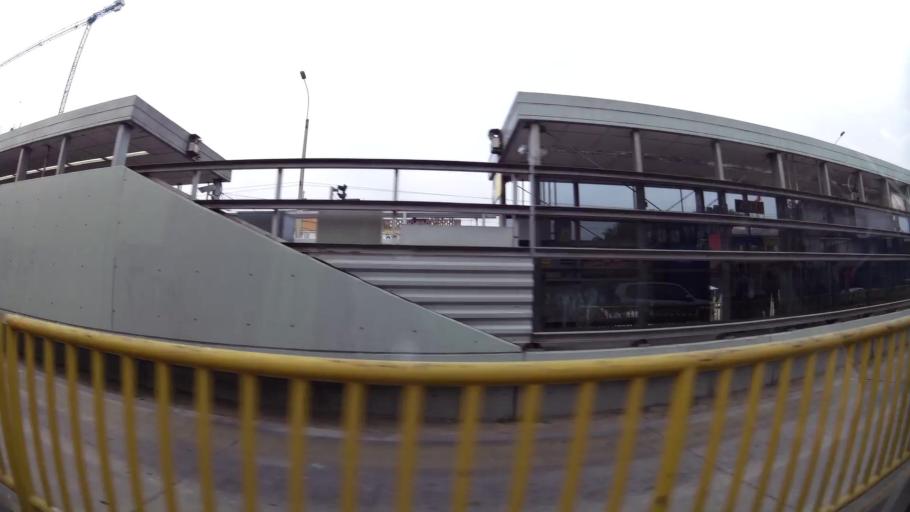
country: PE
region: Lima
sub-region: Lima
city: Surco
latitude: -12.1395
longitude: -77.0177
